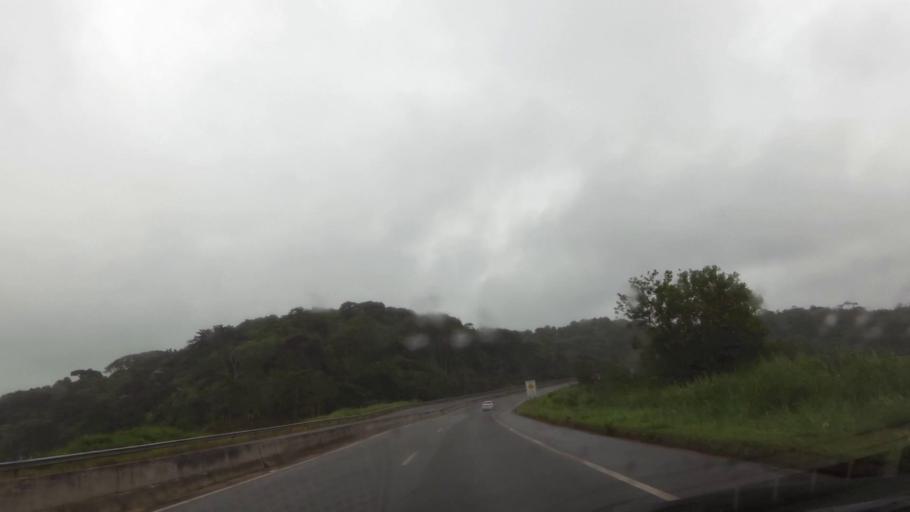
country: BR
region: Espirito Santo
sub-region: Guarapari
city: Guarapari
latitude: -20.6142
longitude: -40.4915
